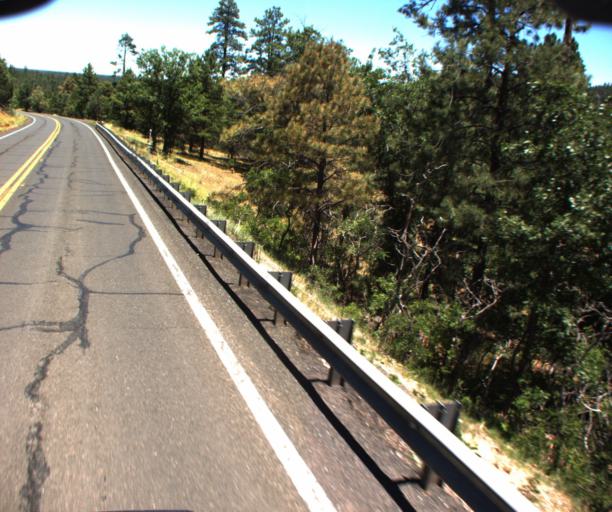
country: US
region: Arizona
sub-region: Gila County
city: Pine
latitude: 34.5981
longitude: -111.2416
